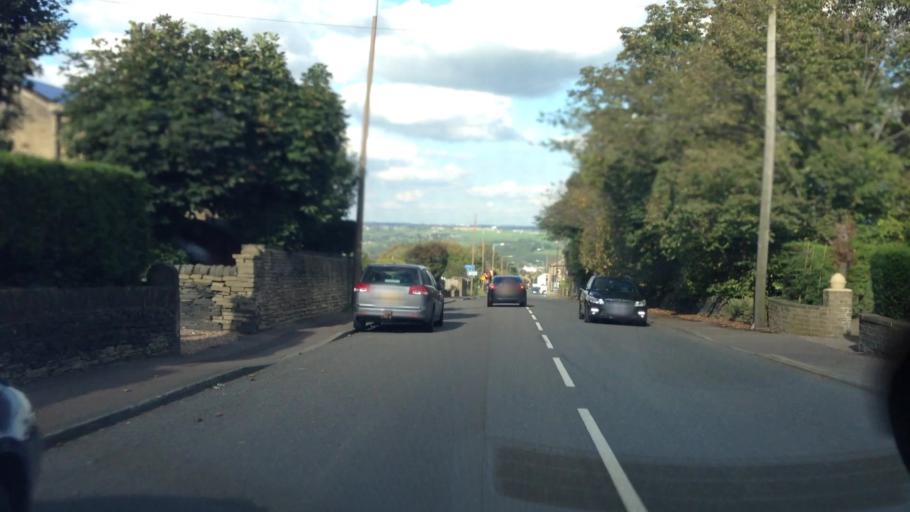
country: GB
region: England
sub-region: Calderdale
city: Brighouse
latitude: 53.6811
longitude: -1.8023
